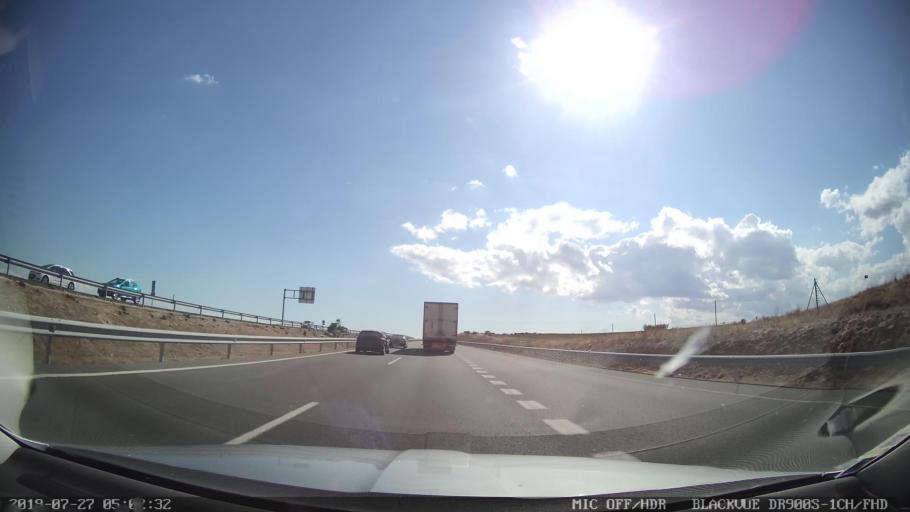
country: ES
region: Castille-La Mancha
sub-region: Province of Toledo
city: Las Ventas de Retamosa
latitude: 40.1759
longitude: -4.1504
